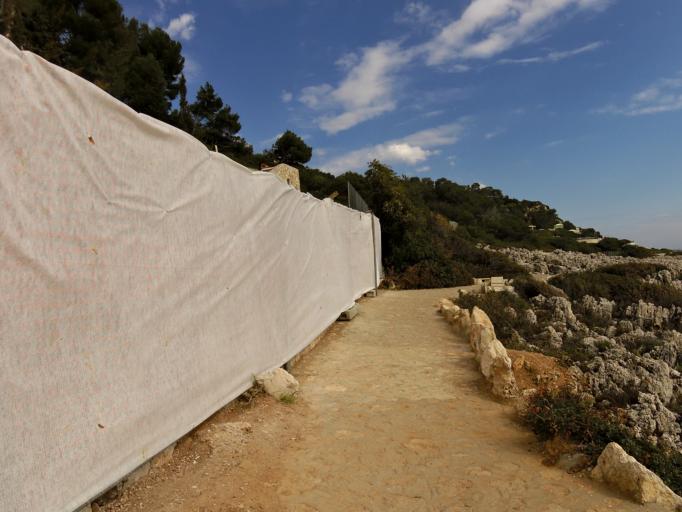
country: FR
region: Provence-Alpes-Cote d'Azur
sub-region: Departement des Alpes-Maritimes
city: Saint-Jean-Cap-Ferrat
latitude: 43.6752
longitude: 7.3288
